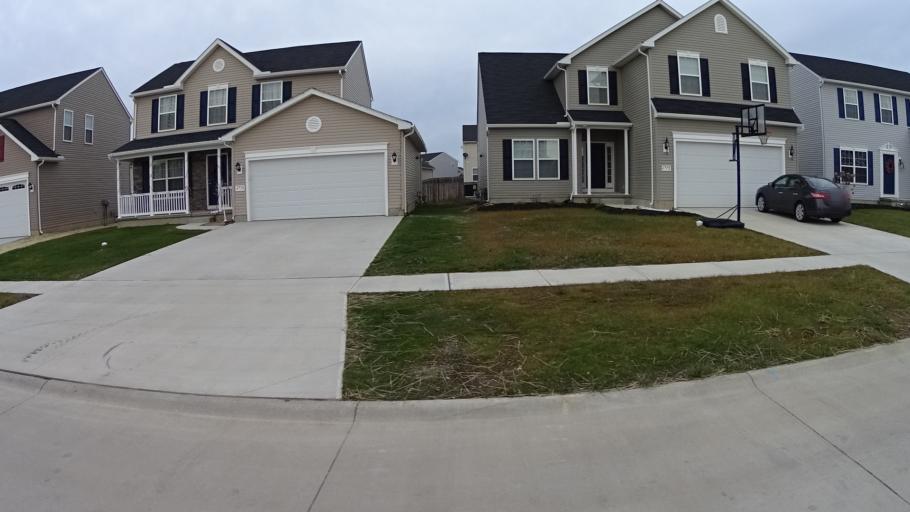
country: US
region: Ohio
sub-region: Lorain County
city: North Ridgeville
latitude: 41.3933
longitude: -82.0402
